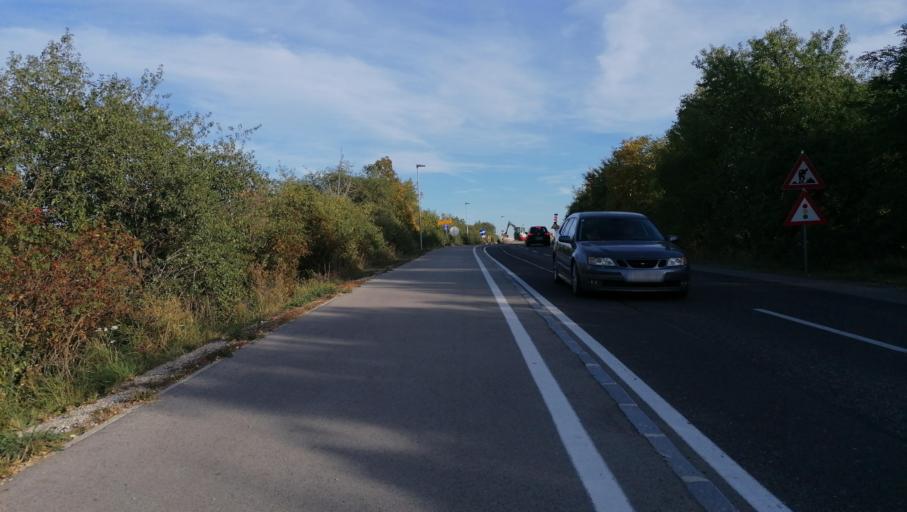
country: AT
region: Lower Austria
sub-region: Politischer Bezirk Baden
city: Pfaffstatten
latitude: 47.9827
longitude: 16.2663
